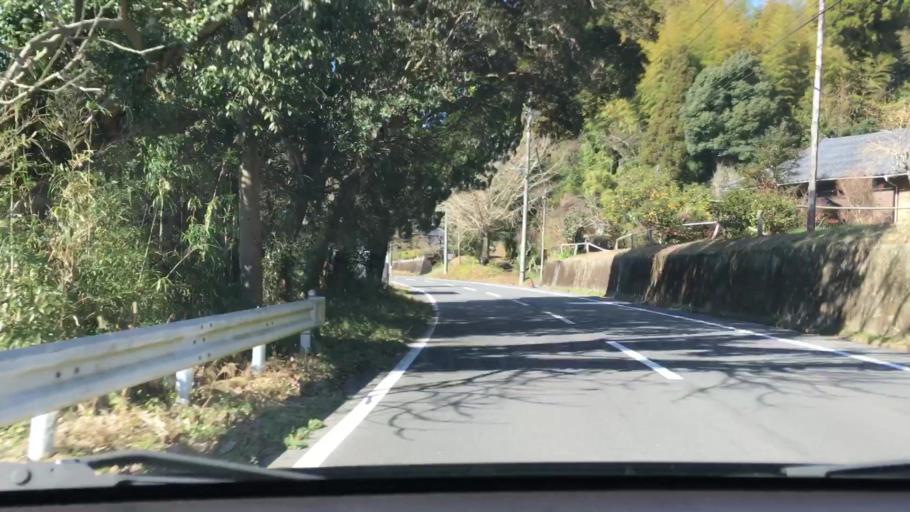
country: JP
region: Kagoshima
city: Ijuin
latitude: 31.7067
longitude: 130.4444
